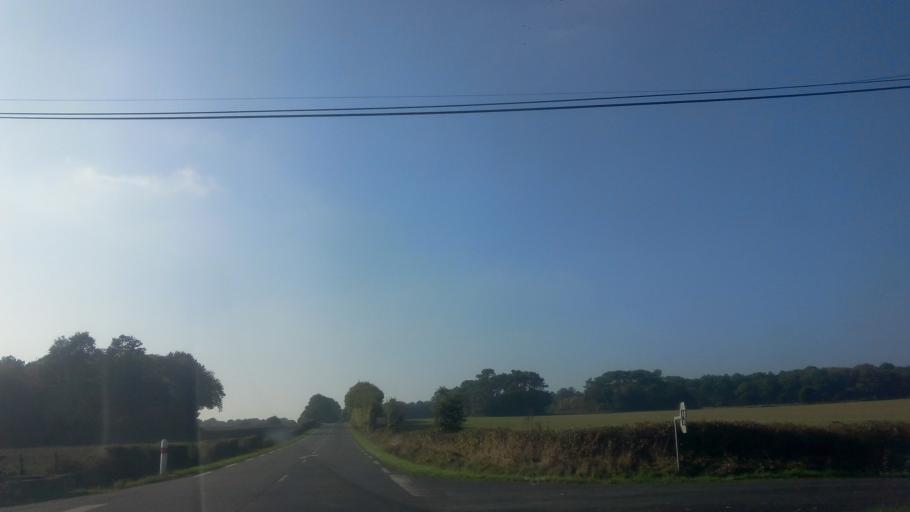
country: FR
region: Pays de la Loire
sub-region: Departement de la Loire-Atlantique
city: Avessac
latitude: 47.6394
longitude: -2.0007
